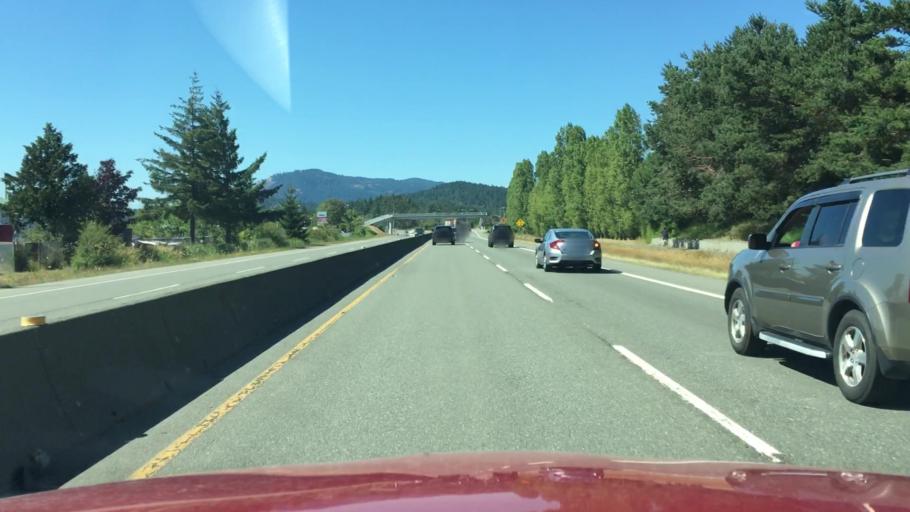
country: CA
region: British Columbia
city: North Saanich
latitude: 48.6591
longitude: -123.4144
